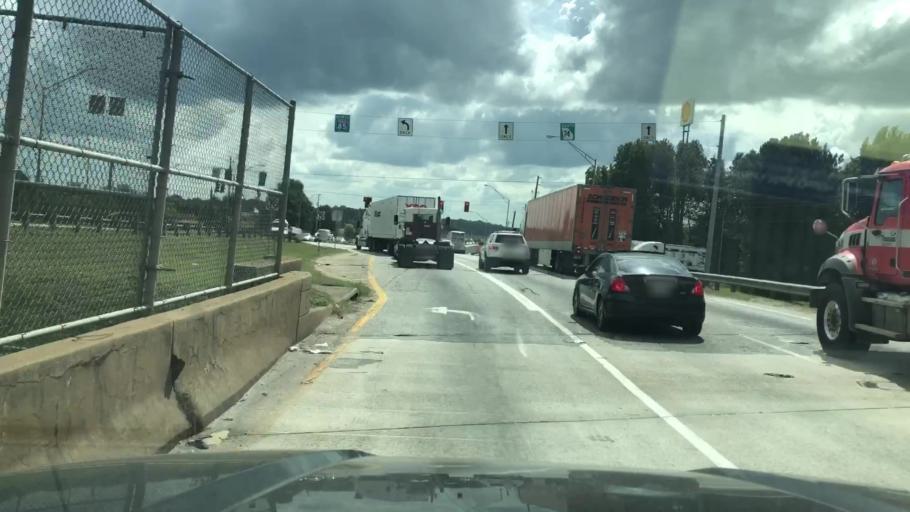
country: US
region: Georgia
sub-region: Fulton County
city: Fairburn
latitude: 33.5458
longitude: -84.5775
